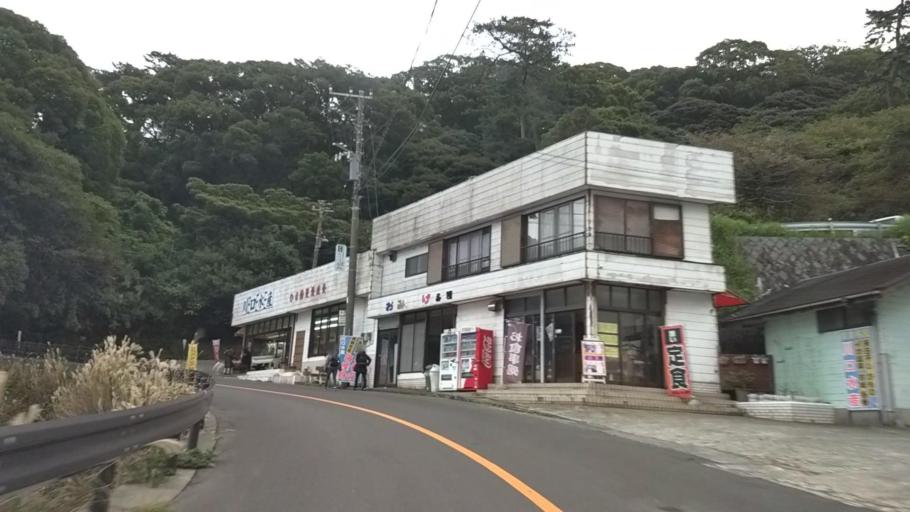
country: JP
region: Kanagawa
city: Yugawara
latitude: 35.1465
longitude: 139.1525
